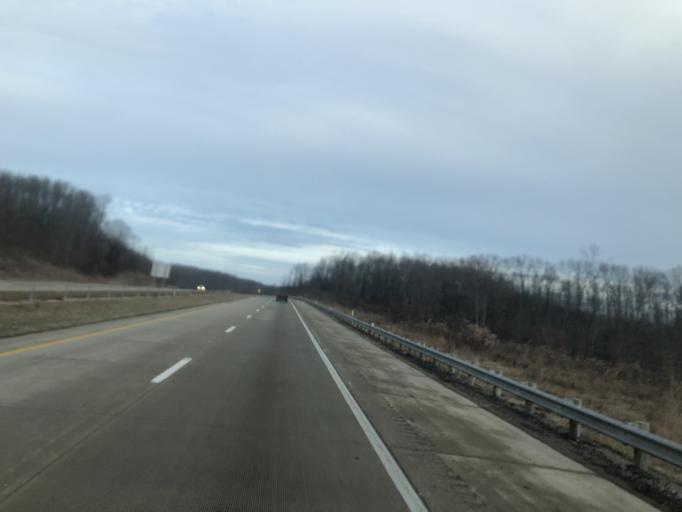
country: US
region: Ohio
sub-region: Athens County
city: Nelsonville
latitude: 39.4596
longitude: -82.2156
